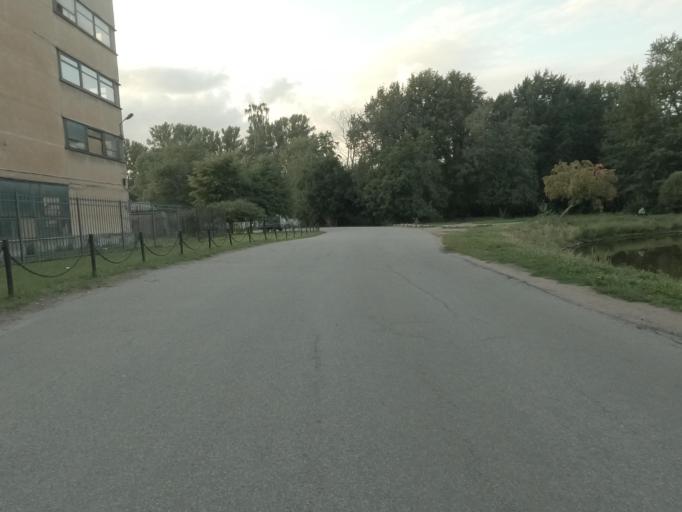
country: RU
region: St.-Petersburg
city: Admiralteisky
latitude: 59.8982
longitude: 30.2609
